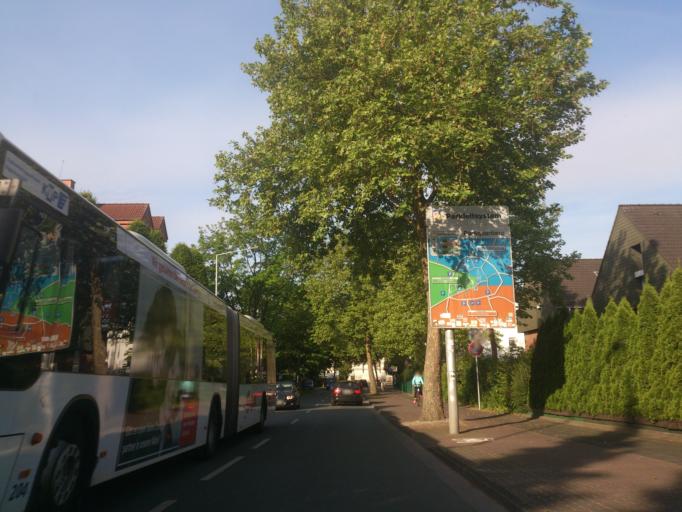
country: DE
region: North Rhine-Westphalia
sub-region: Regierungsbezirk Detmold
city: Paderborn
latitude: 51.7224
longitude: 8.7670
